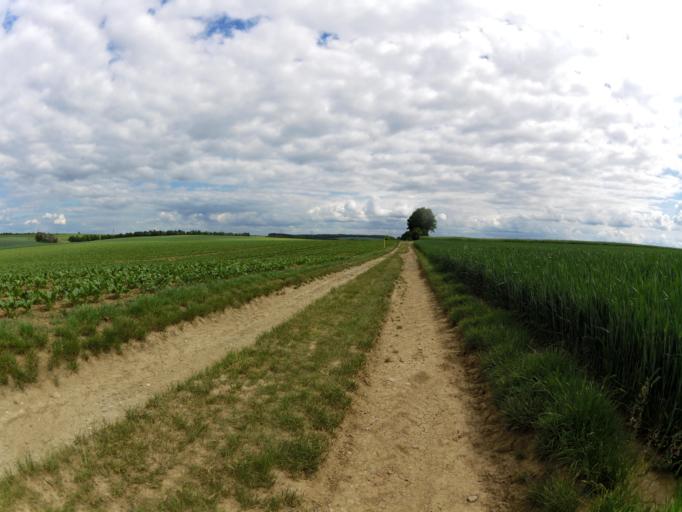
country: DE
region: Bavaria
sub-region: Regierungsbezirk Unterfranken
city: Gaukonigshofen
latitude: 49.6639
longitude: 10.0133
